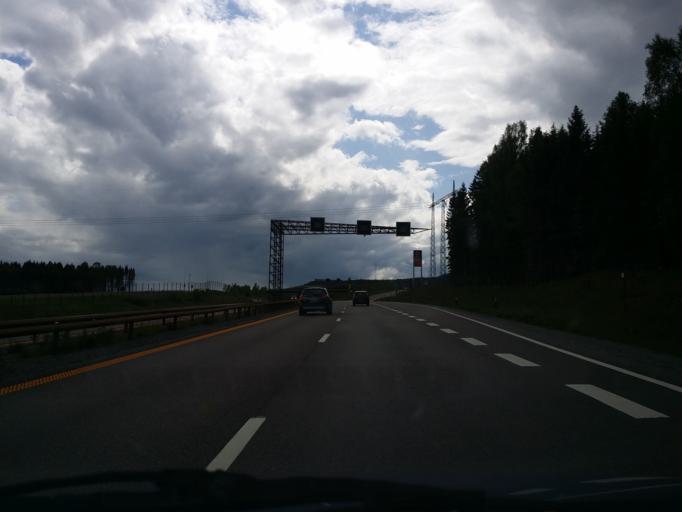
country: NO
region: Akershus
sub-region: Eidsvoll
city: Eidsvoll
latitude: 60.3922
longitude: 11.2191
